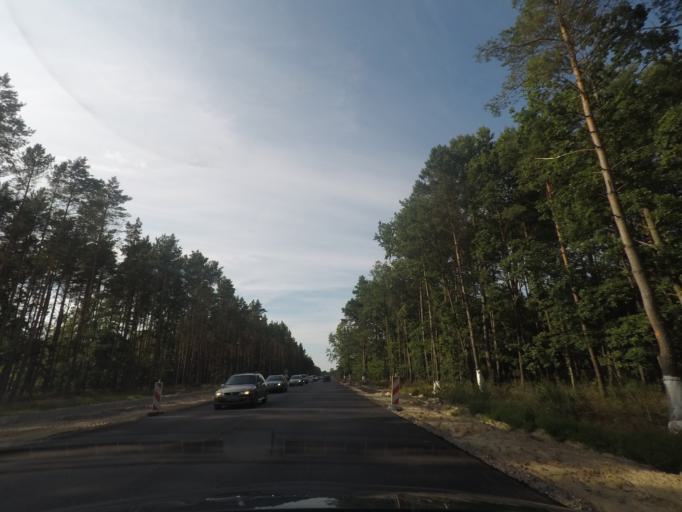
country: PL
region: Pomeranian Voivodeship
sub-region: Powiat leborski
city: Leba
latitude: 54.7163
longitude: 17.5761
